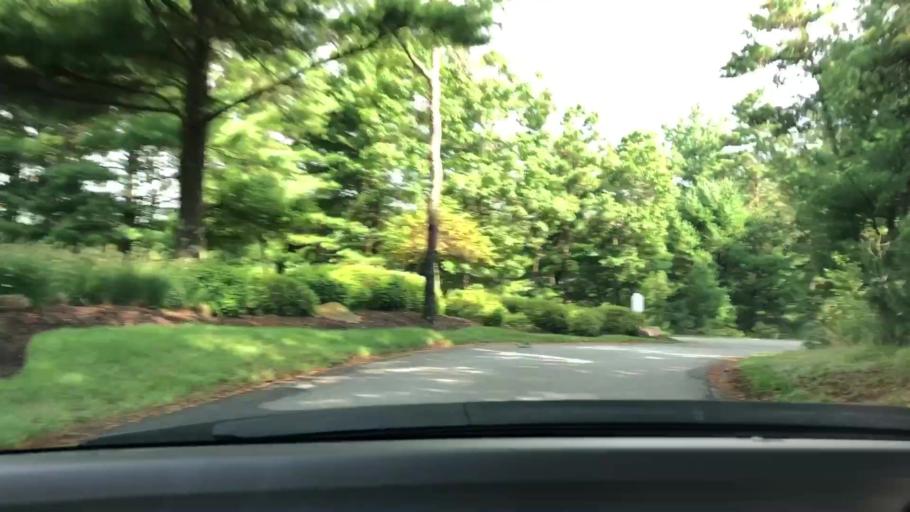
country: US
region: Massachusetts
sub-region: Plymouth County
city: White Island Shores
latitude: 41.8889
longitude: -70.5849
